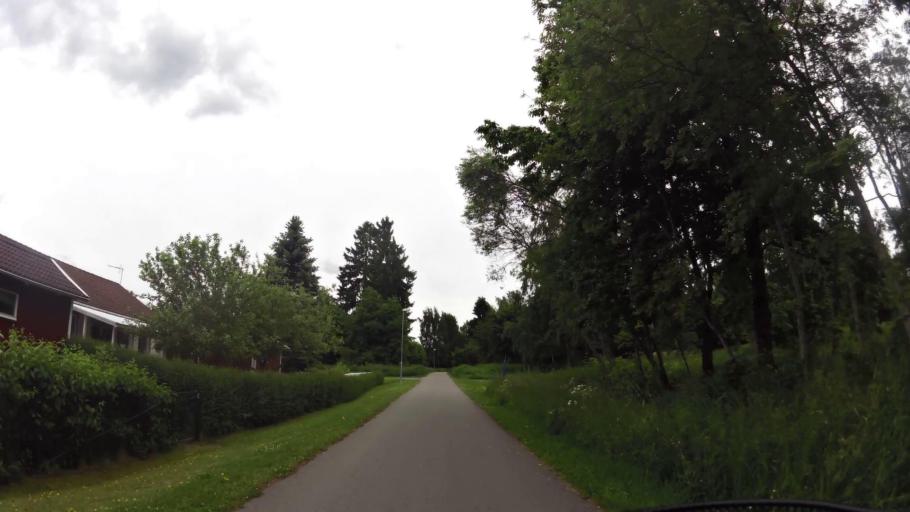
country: SE
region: OEstergoetland
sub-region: Linkopings Kommun
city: Malmslatt
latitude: 58.3795
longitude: 15.5628
